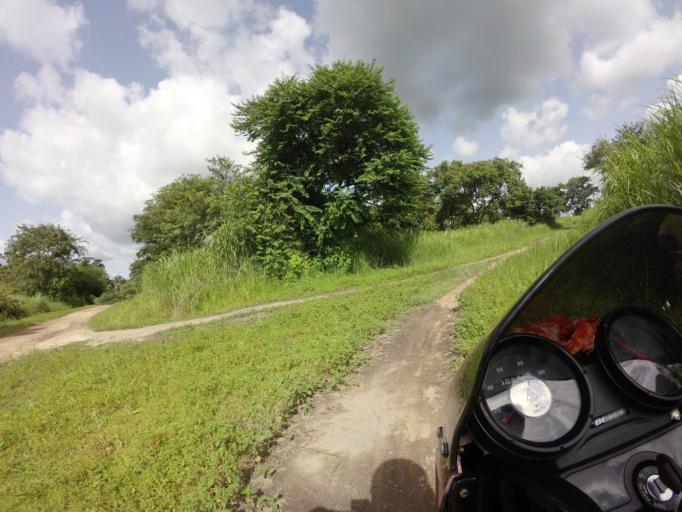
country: SL
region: Eastern Province
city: Tombu
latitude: 8.5556
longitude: -10.7221
